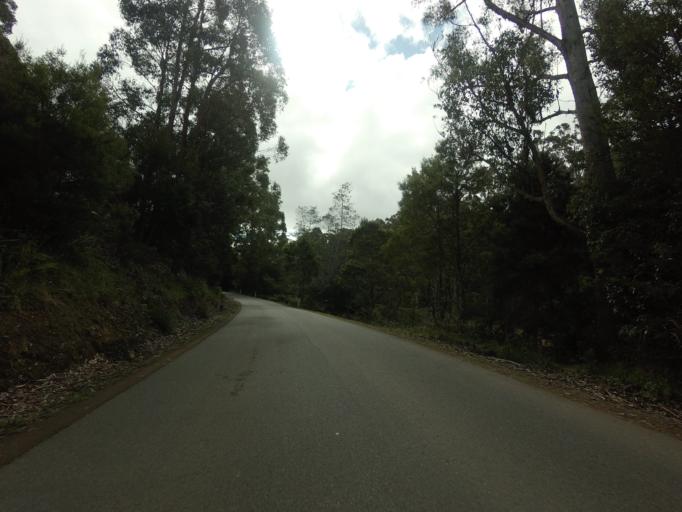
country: AU
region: Tasmania
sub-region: Huon Valley
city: Geeveston
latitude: -43.4163
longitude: 146.9645
